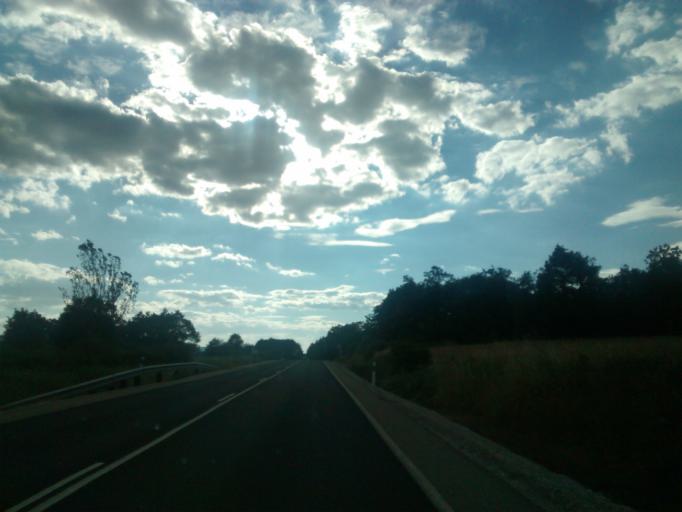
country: ES
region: Castille and Leon
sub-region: Provincia de Burgos
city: Basconcillos del Tozo
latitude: 42.6823
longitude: -3.9538
